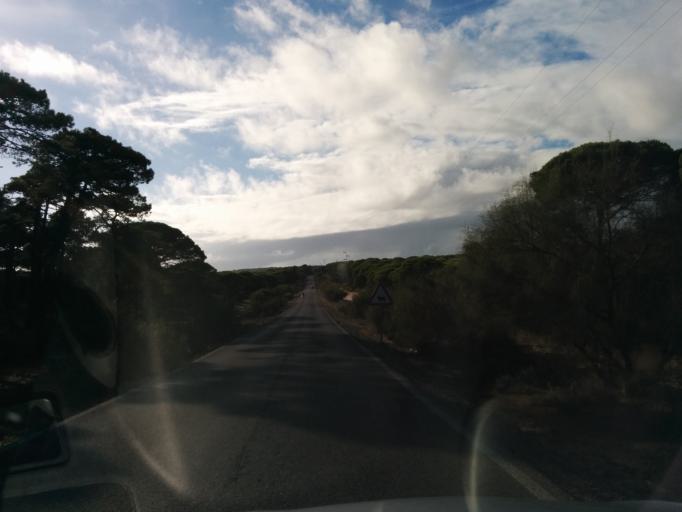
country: ES
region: Andalusia
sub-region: Provincia de Cadiz
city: Vejer de la Frontera
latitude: 36.1923
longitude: -5.9852
